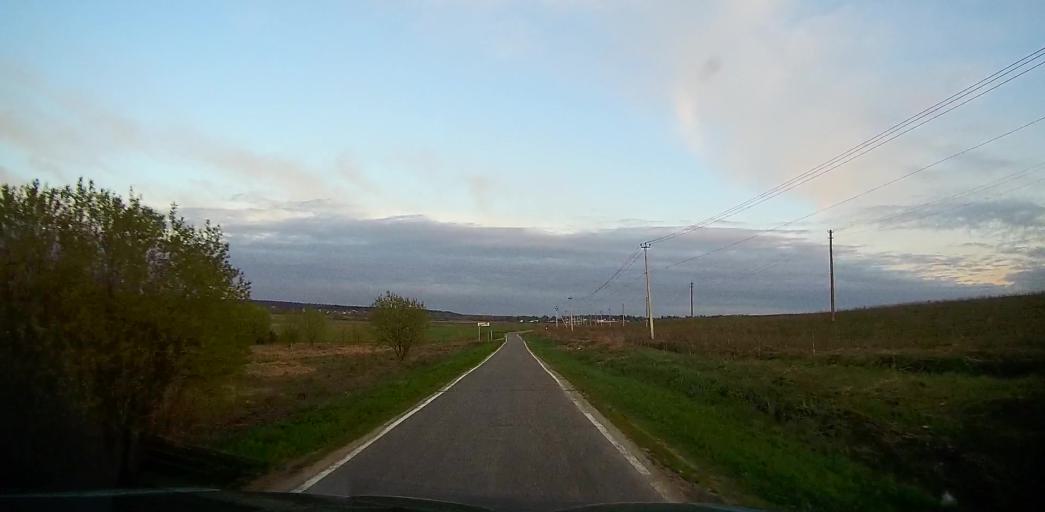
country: RU
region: Moskovskaya
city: Peski
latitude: 55.2268
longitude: 38.7346
